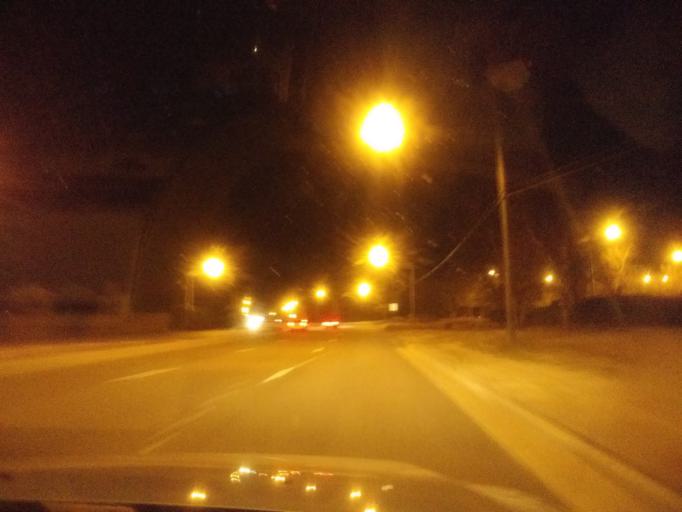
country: US
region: Virginia
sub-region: City of Chesapeake
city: Chesapeake
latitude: 36.7770
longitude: -76.1980
